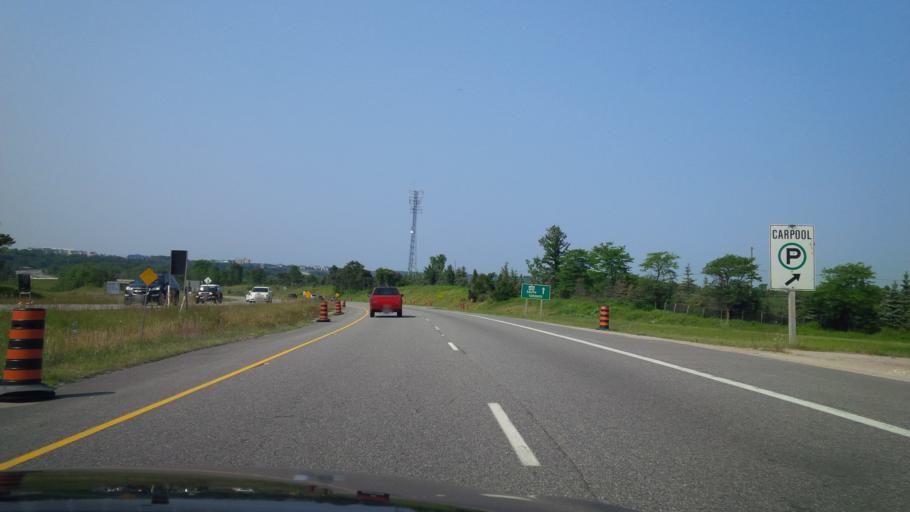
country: CA
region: Ontario
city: Barrie
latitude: 44.4342
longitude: -79.6453
